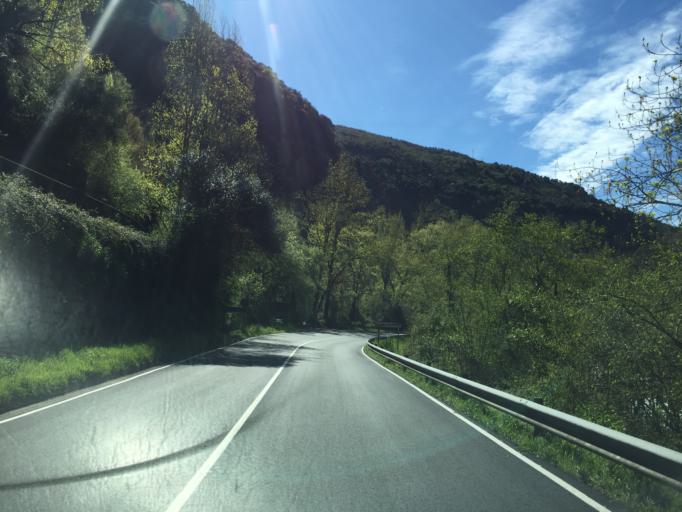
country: ES
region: Asturias
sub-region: Province of Asturias
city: Proaza
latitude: 43.3096
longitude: -5.9872
